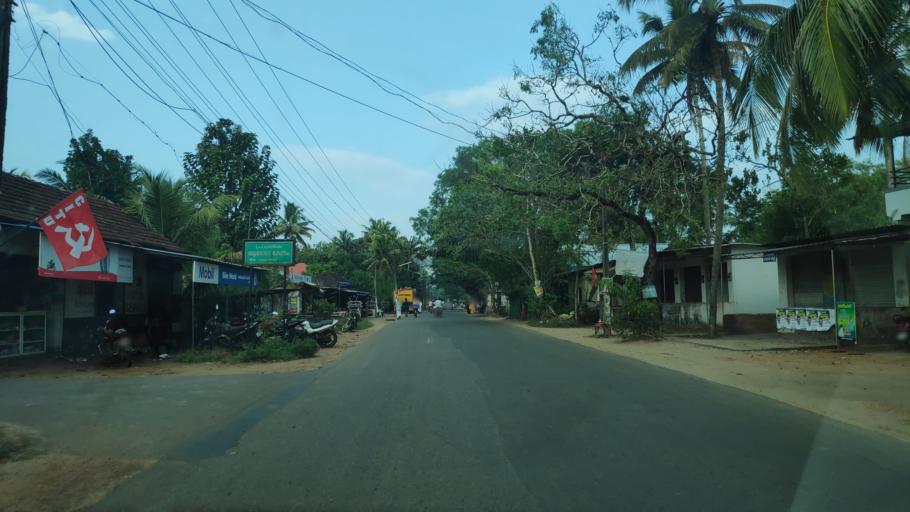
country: IN
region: Kerala
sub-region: Alappuzha
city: Alleppey
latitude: 9.5611
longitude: 76.3450
